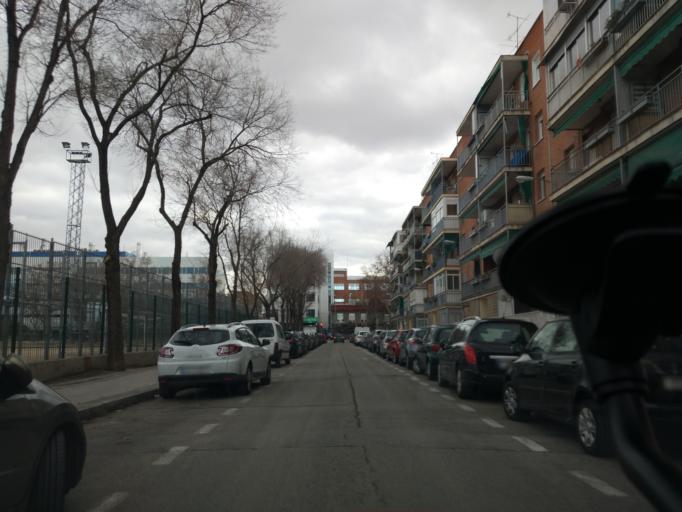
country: ES
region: Madrid
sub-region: Provincia de Madrid
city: San Blas
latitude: 40.4417
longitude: -3.6286
